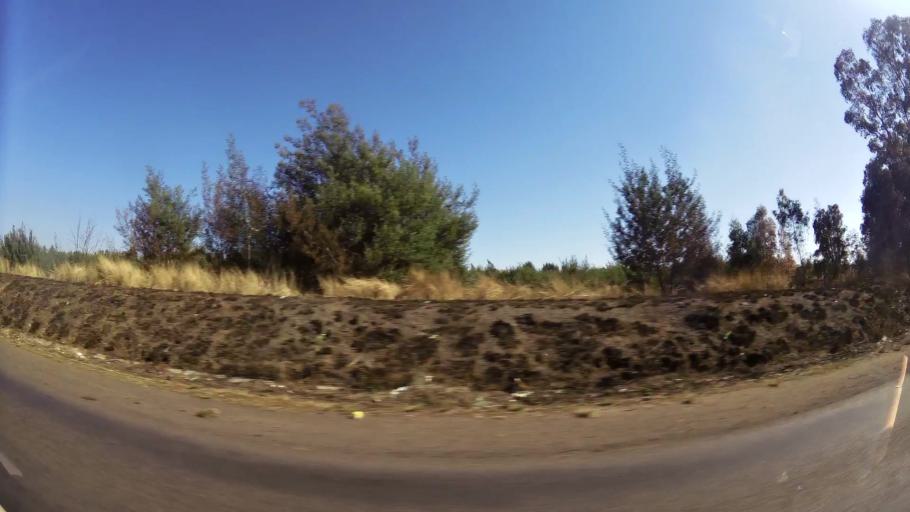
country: ZA
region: Mpumalanga
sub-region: Nkangala District Municipality
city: Witbank
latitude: -25.8458
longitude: 29.2366
